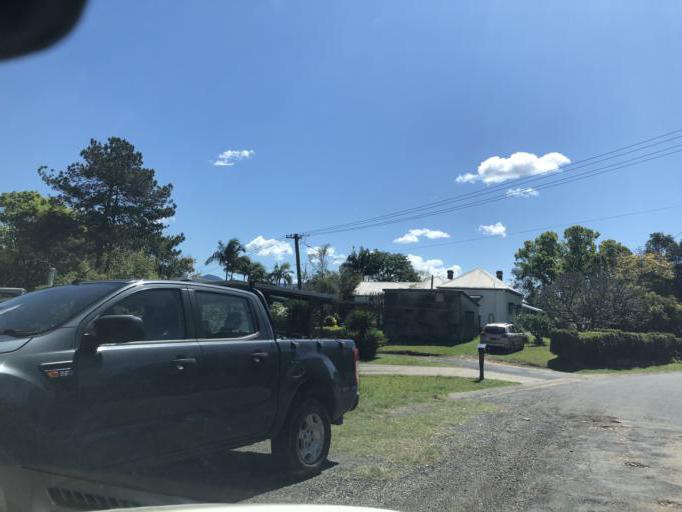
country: AU
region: New South Wales
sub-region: Bellingen
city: Bellingen
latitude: -30.4592
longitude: 152.8976
